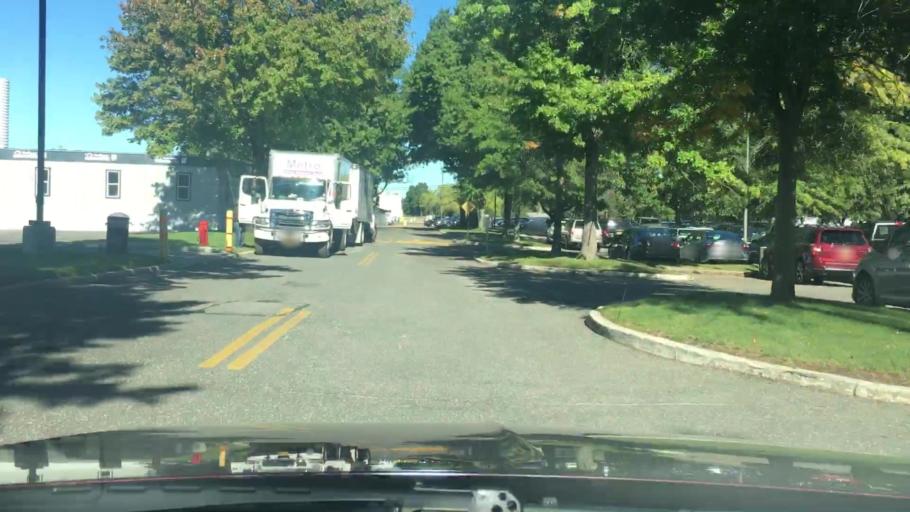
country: US
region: New York
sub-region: Suffolk County
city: Melville
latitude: 40.7778
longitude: -73.4069
